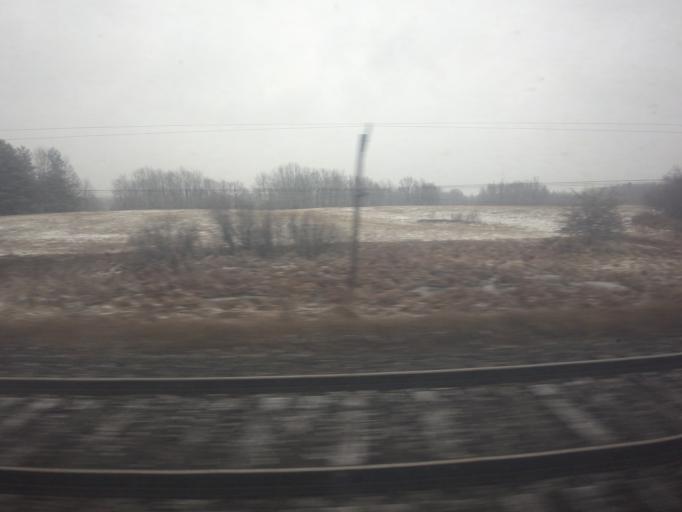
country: CA
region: Ontario
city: Brockville
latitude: 44.5642
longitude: -75.7790
